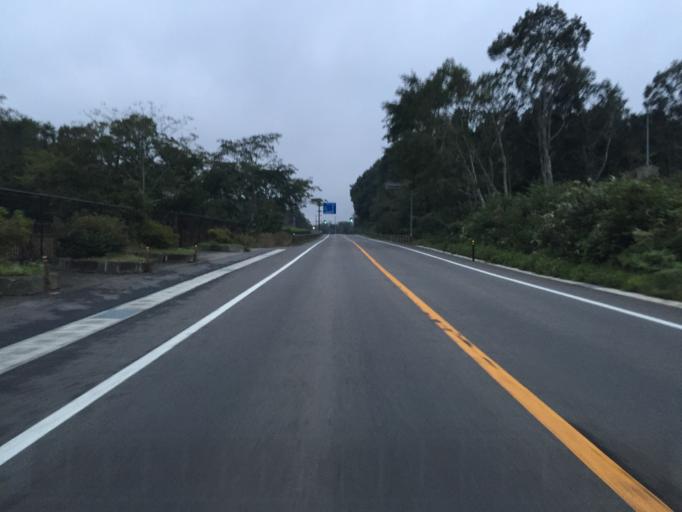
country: JP
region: Fukushima
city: Inawashiro
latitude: 37.5184
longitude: 140.0208
